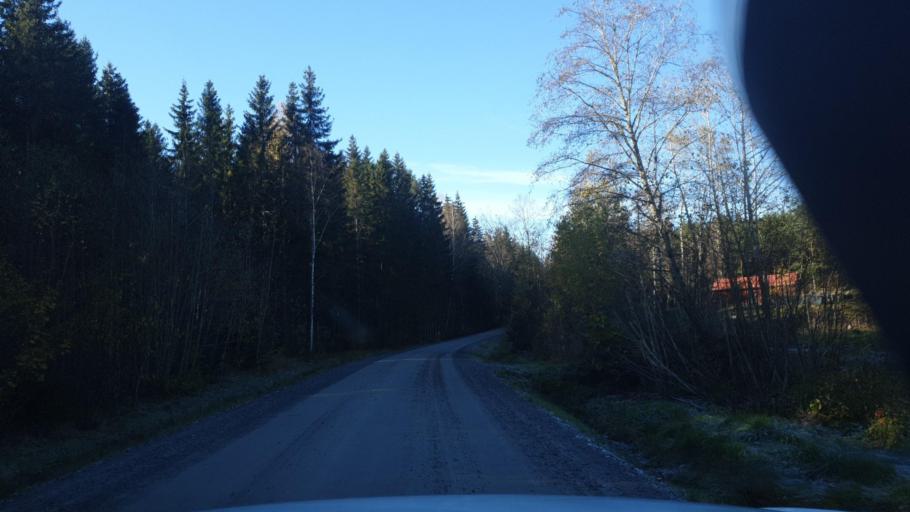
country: SE
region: Vaermland
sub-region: Karlstads Kommun
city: Edsvalla
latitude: 59.4418
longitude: 13.1912
